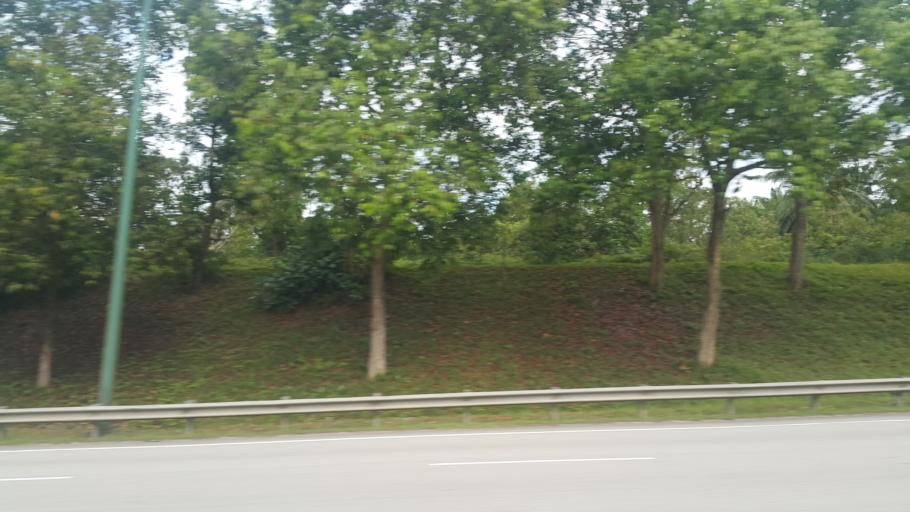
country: MY
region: Johor
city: Pekan Nenas
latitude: 1.4056
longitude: 103.5908
